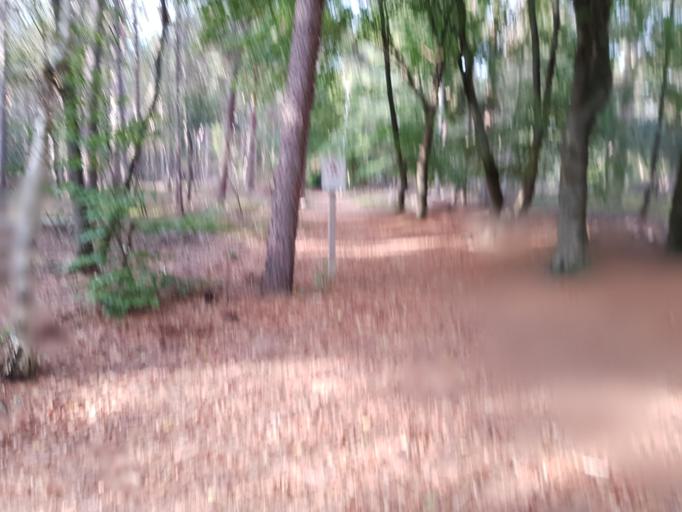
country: NL
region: Gelderland
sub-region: Gemeente Nunspeet
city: Nunspeet
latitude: 52.3419
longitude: 5.7133
